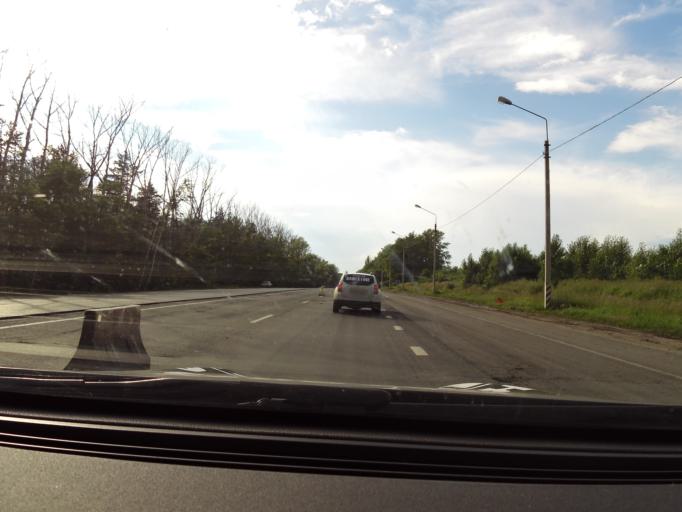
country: RU
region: Vladimir
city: Novovyazniki
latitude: 56.1868
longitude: 42.3959
